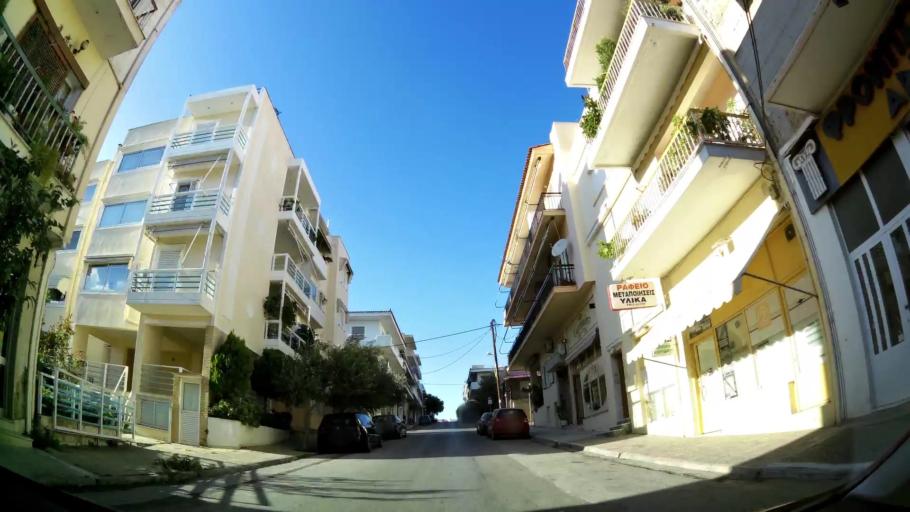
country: GR
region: Attica
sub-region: Nomarchia Anatolikis Attikis
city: Rafina
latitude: 38.0232
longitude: 24.0062
